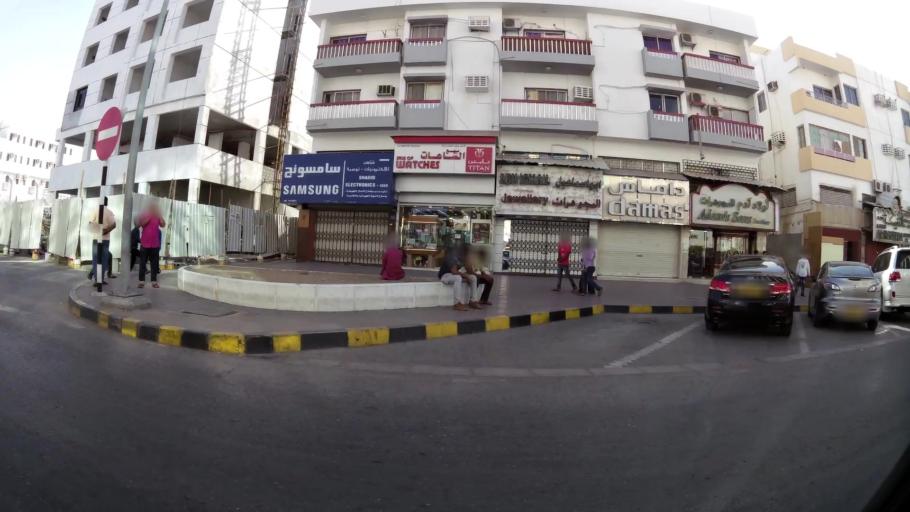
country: OM
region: Muhafazat Masqat
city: Muscat
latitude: 23.5911
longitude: 58.5448
